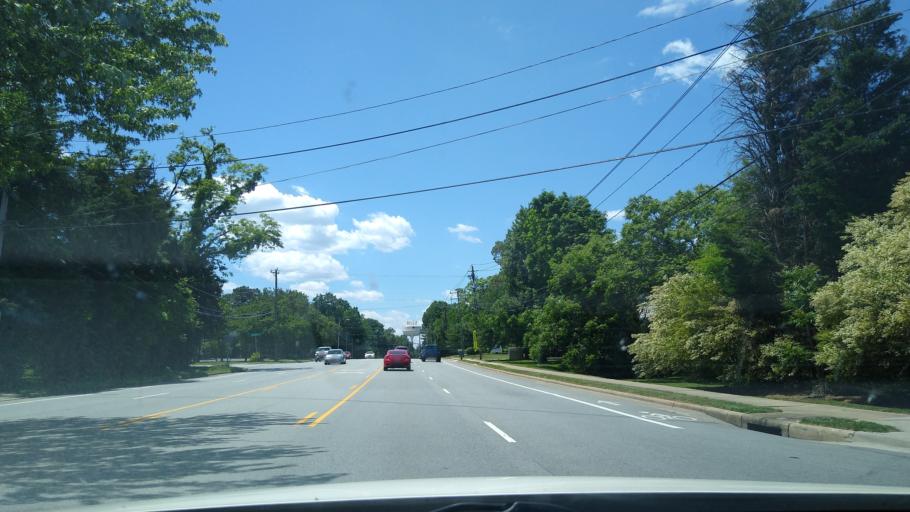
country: US
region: North Carolina
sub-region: Guilford County
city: Greensboro
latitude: 36.0914
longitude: -79.8737
